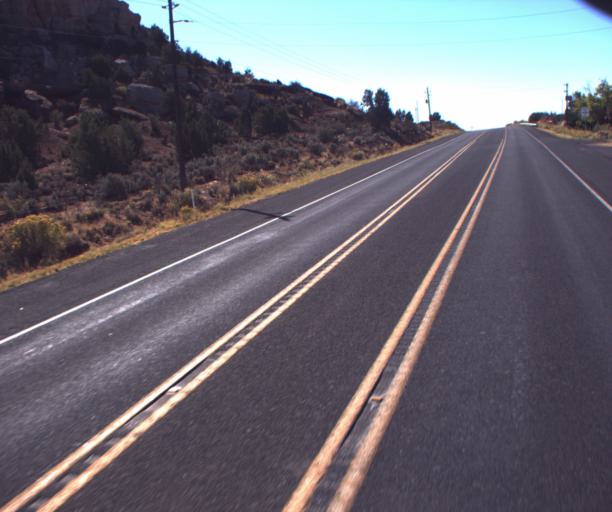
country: US
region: Arizona
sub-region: Coconino County
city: Fredonia
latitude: 36.9949
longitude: -112.5305
